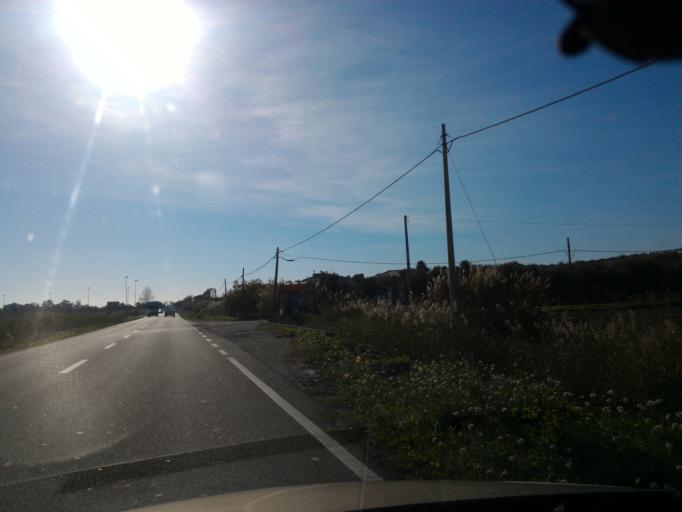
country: IT
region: Calabria
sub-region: Provincia di Crotone
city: Tronca
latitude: 39.2173
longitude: 17.1058
